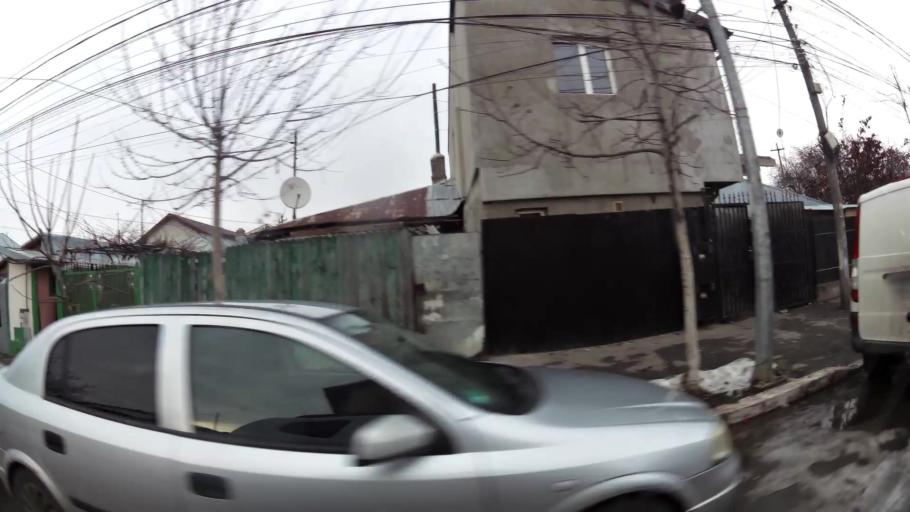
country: RO
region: Ilfov
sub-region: Voluntari City
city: Voluntari
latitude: 44.4802
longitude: 26.1831
